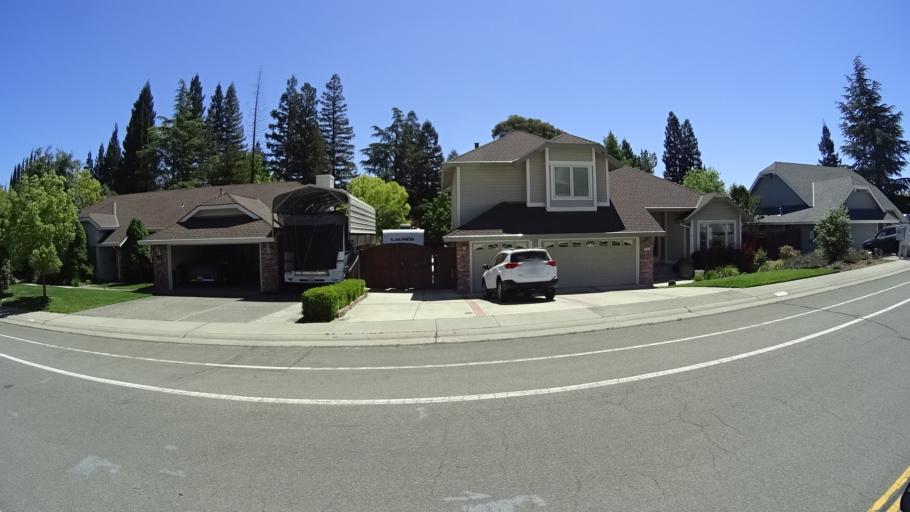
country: US
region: California
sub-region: Placer County
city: Rocklin
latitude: 38.8048
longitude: -121.2332
